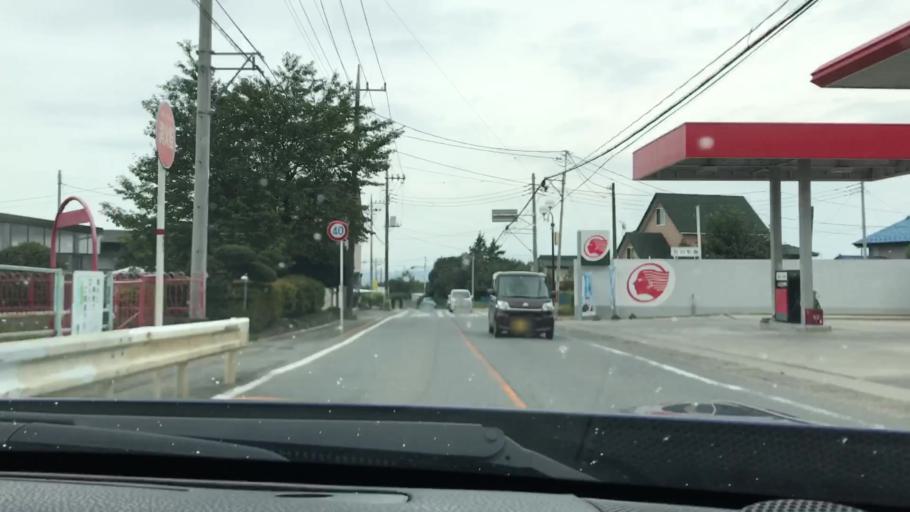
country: JP
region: Gunma
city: Kanekomachi
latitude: 36.3936
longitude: 138.9603
